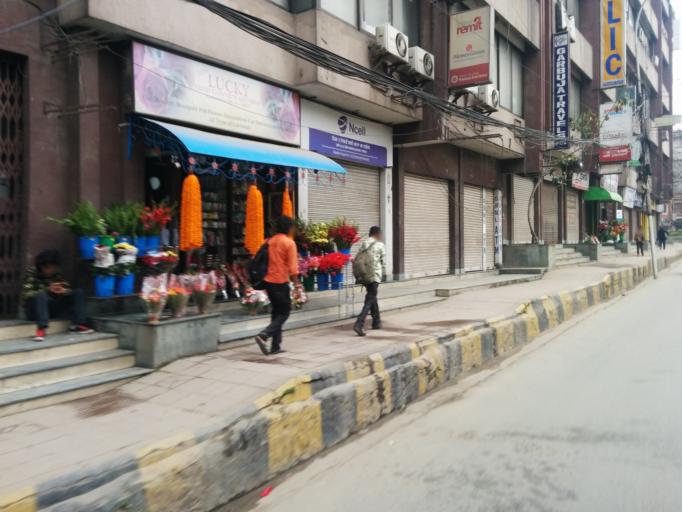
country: NP
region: Central Region
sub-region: Bagmati Zone
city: Kathmandu
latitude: 27.7090
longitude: 85.3219
